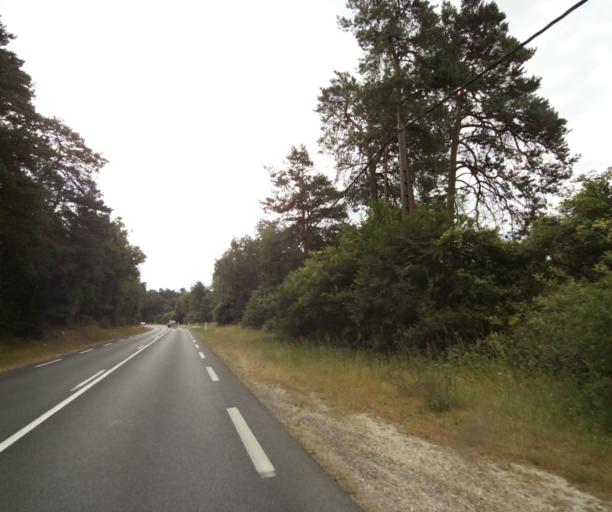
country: FR
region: Ile-de-France
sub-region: Departement de Seine-et-Marne
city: Arbonne-la-Foret
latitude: 48.4014
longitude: 2.5476
